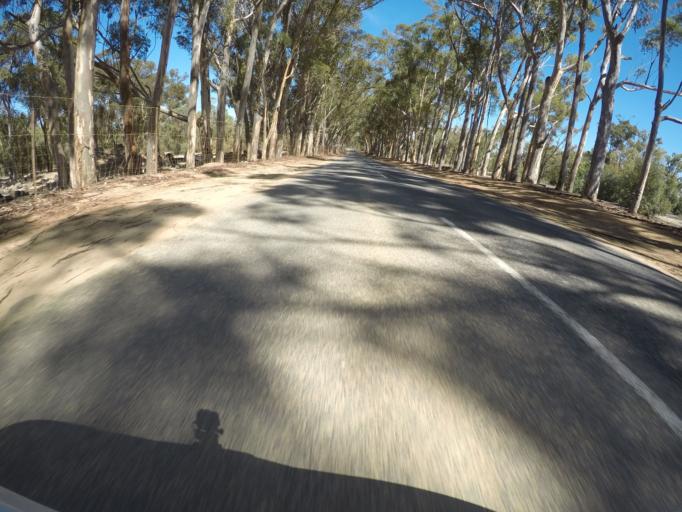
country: ZA
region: Western Cape
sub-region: City of Cape Town
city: Sunset Beach
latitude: -33.7648
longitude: 18.5508
